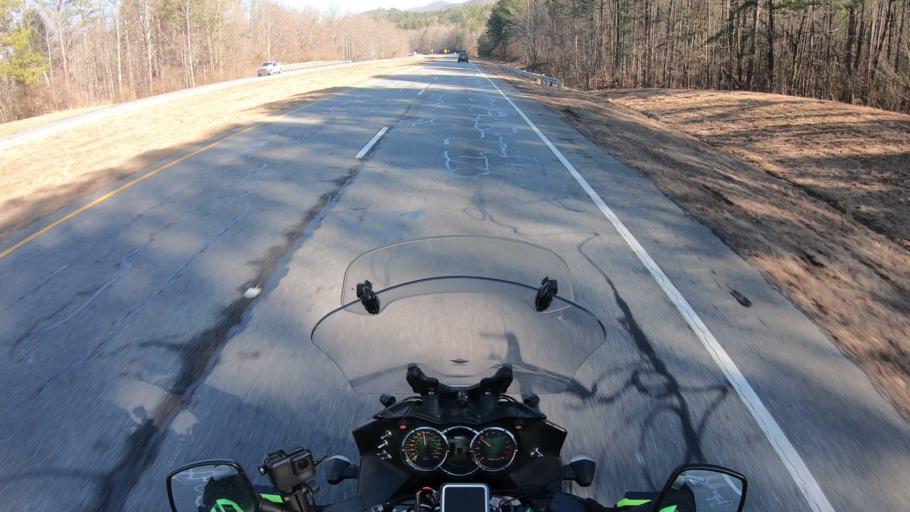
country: US
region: Georgia
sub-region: Gilmer County
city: Ellijay
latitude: 34.7247
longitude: -84.4417
